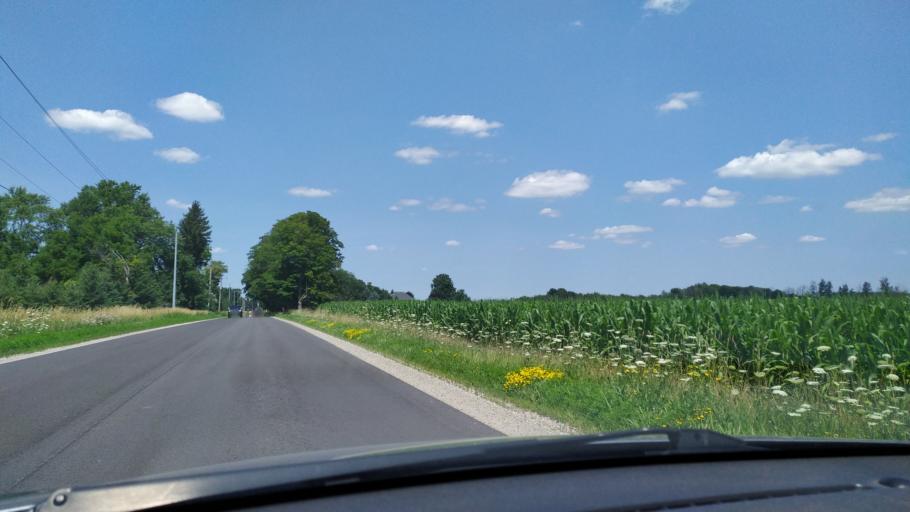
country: CA
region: Ontario
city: Stratford
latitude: 43.3561
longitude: -80.9378
